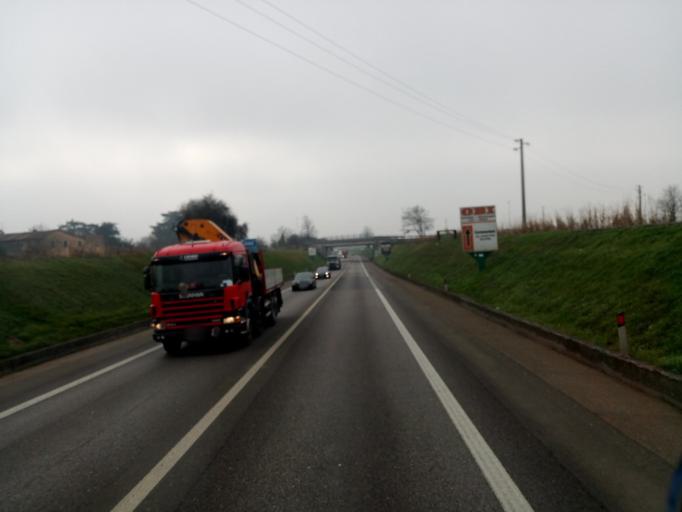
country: IT
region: Lombardy
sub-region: Provincia di Brescia
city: Castenedolo
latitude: 45.4718
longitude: 10.3178
